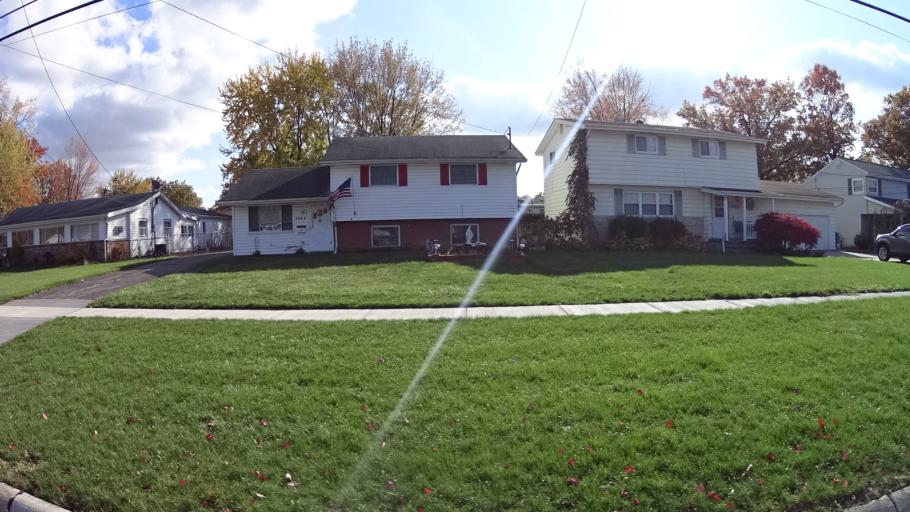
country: US
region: Ohio
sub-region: Lorain County
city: Sheffield
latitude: 41.4359
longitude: -82.1292
